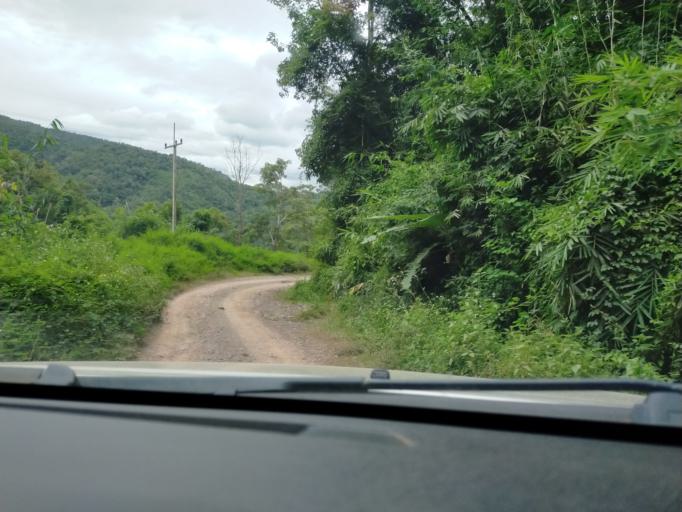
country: TH
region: Nan
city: Chaloem Phra Kiat
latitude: 19.8083
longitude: 101.3626
